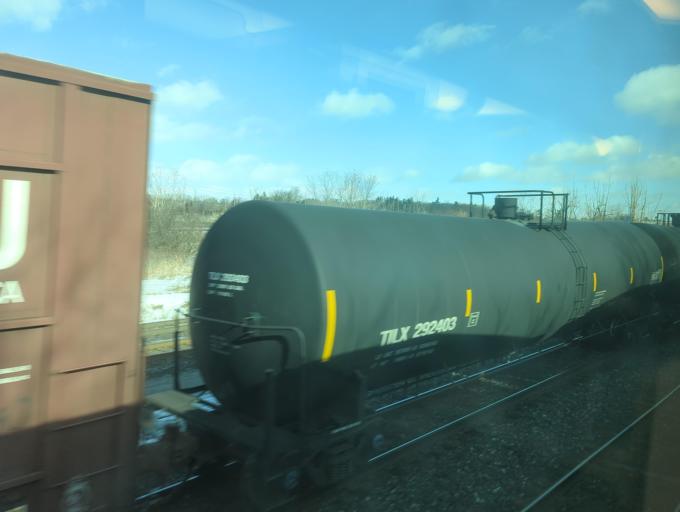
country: CA
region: Ontario
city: Hamilton
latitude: 43.3088
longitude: -79.8619
